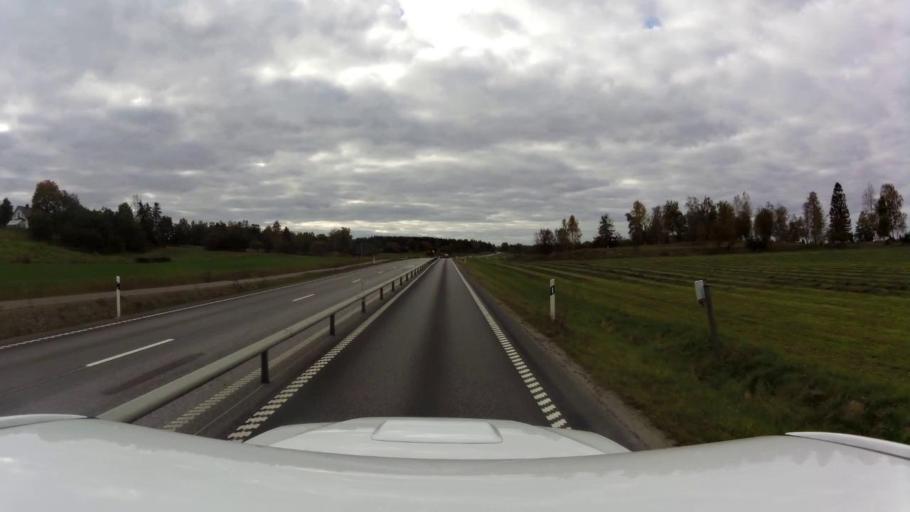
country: SE
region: OEstergoetland
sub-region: Linkopings Kommun
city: Malmslatt
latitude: 58.3123
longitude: 15.5671
